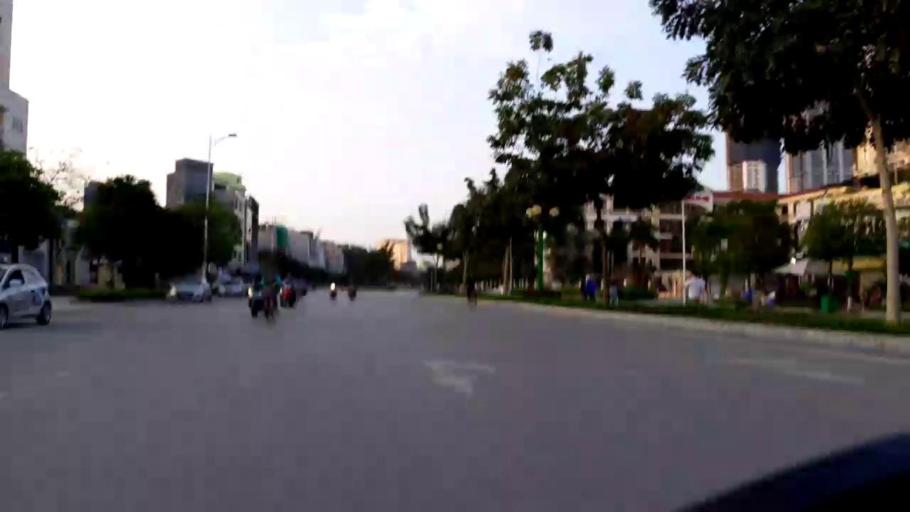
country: VN
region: Ha Noi
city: Cau Giay
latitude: 21.0384
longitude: 105.7978
